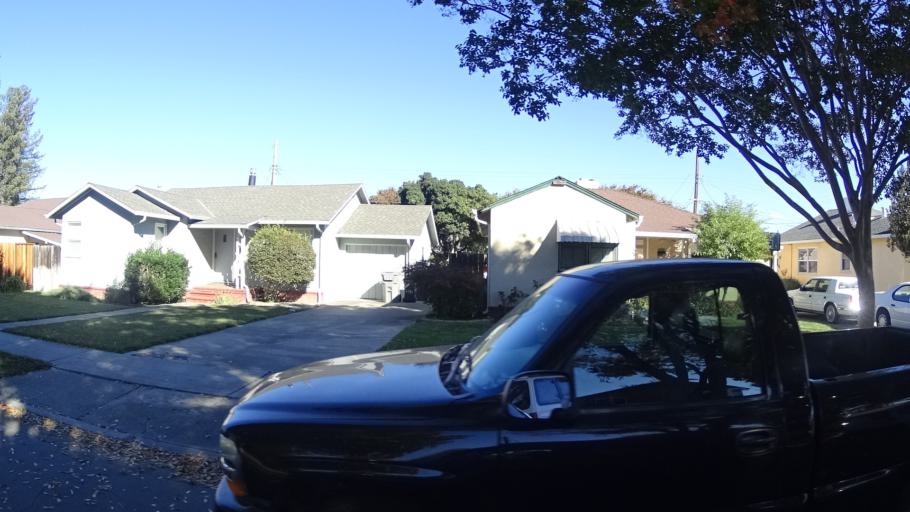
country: US
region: California
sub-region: Santa Clara County
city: San Jose
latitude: 37.3609
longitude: -121.9131
